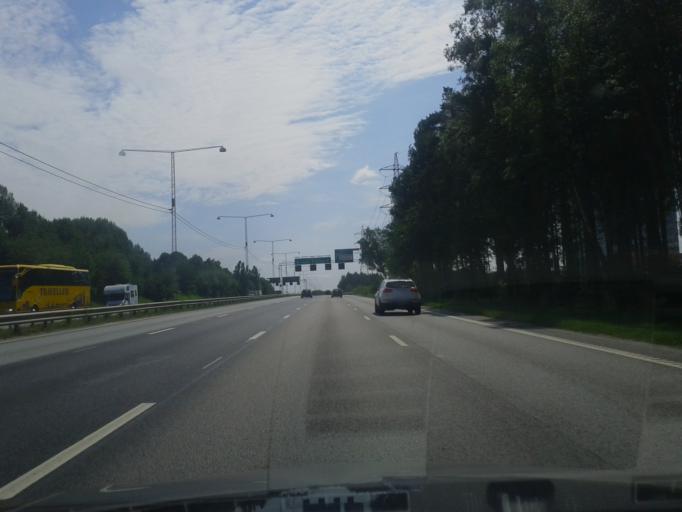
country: SE
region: Stockholm
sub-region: Stockholms Kommun
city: Kista
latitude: 59.4096
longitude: 17.9549
